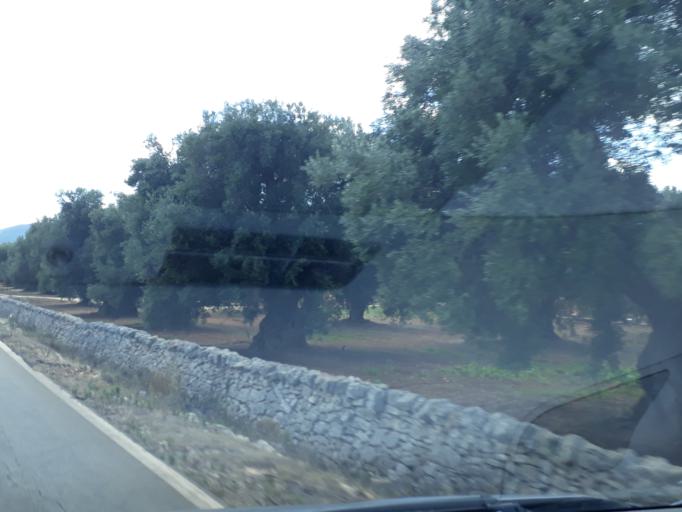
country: IT
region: Apulia
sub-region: Provincia di Brindisi
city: Pezze di Greco
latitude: 40.8075
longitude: 17.3894
